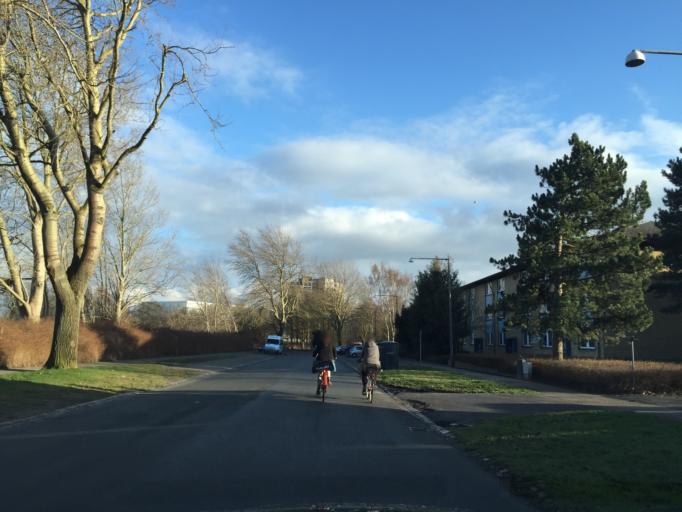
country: DK
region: South Denmark
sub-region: Odense Kommune
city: Neder Holluf
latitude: 55.3771
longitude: 10.4250
